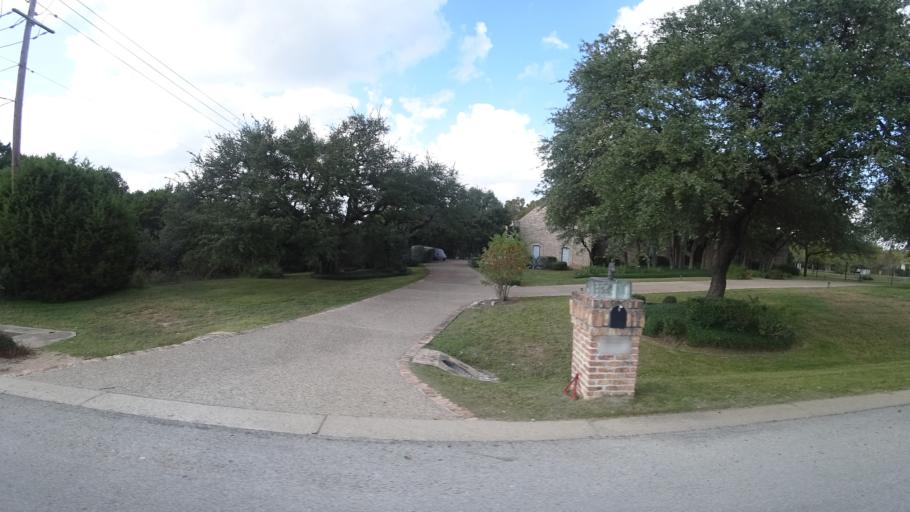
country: US
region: Texas
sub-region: Travis County
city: Barton Creek
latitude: 30.2818
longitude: -97.8817
